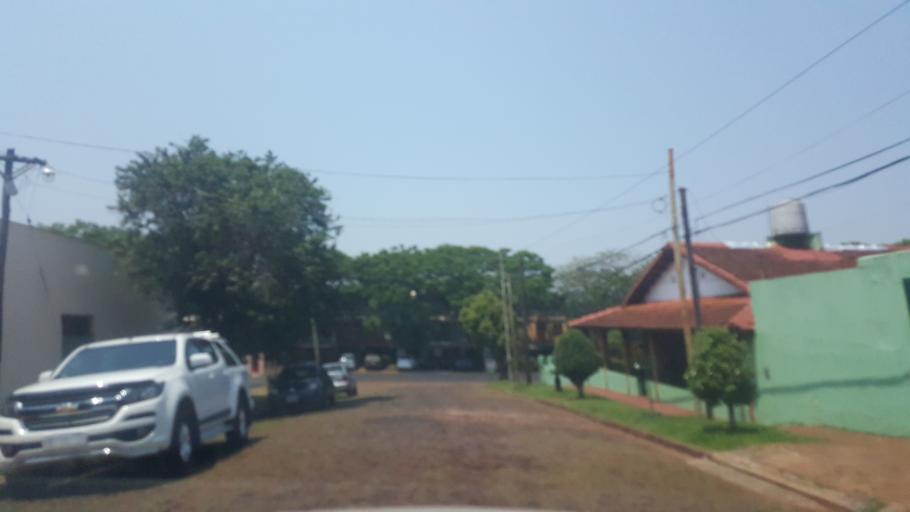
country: AR
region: Misiones
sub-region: Departamento de Capital
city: Posadas
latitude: -27.3943
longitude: -55.9096
